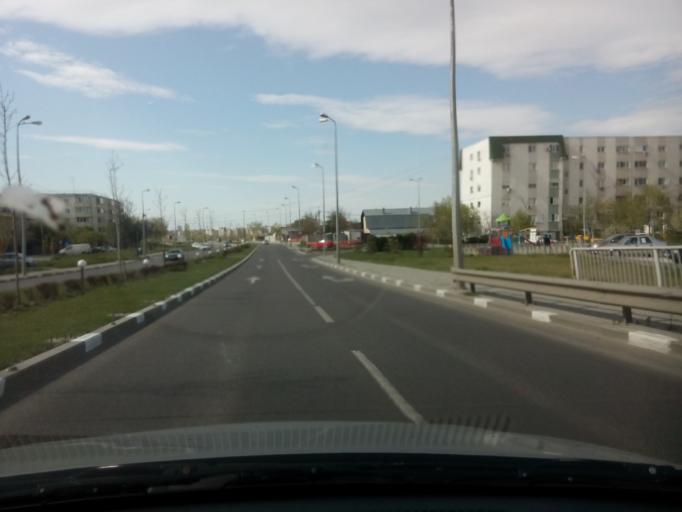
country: RO
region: Ilfov
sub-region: Comuna Fundeni-Dobroesti
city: Fundeni
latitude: 44.4509
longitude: 26.1525
